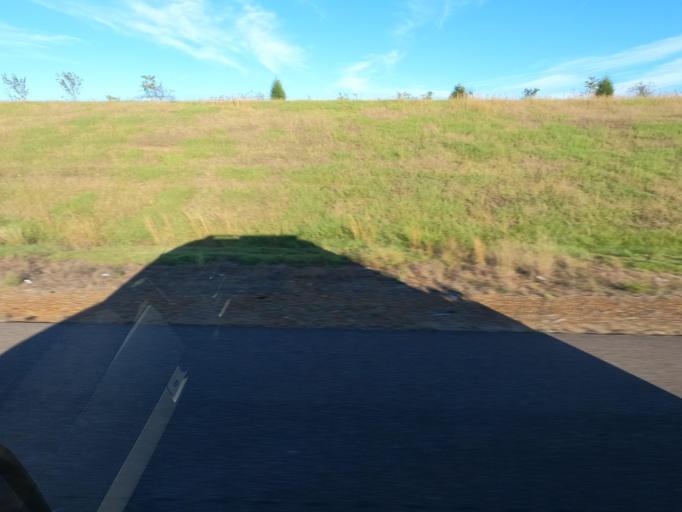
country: US
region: Tennessee
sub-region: Fayette County
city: Piperton
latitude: 35.1118
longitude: -89.6366
